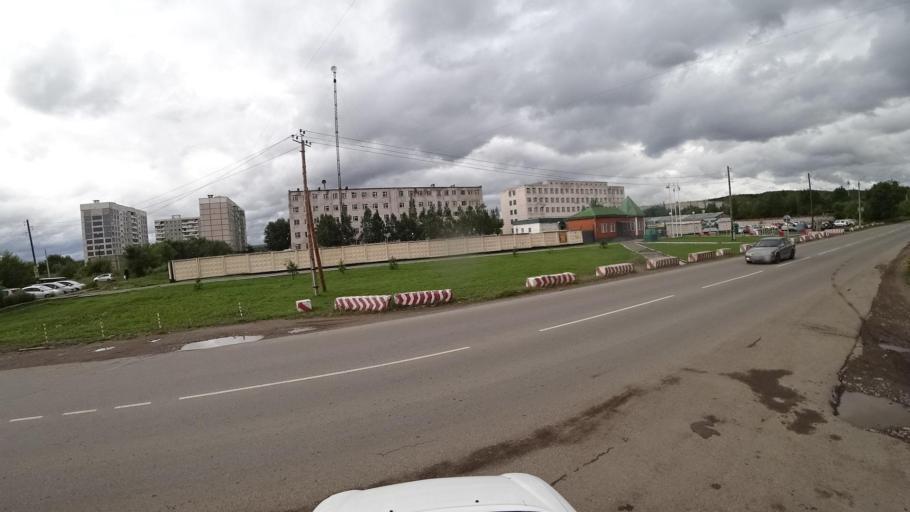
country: RU
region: Khabarovsk Krai
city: Solnechnyy
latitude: 50.5950
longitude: 137.0379
